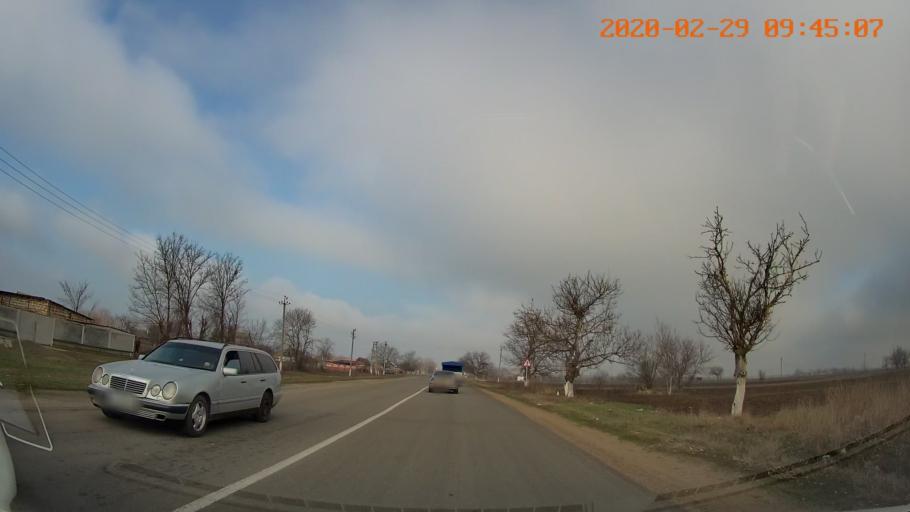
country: MD
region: Telenesti
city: Crasnoe
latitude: 46.6582
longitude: 29.8122
